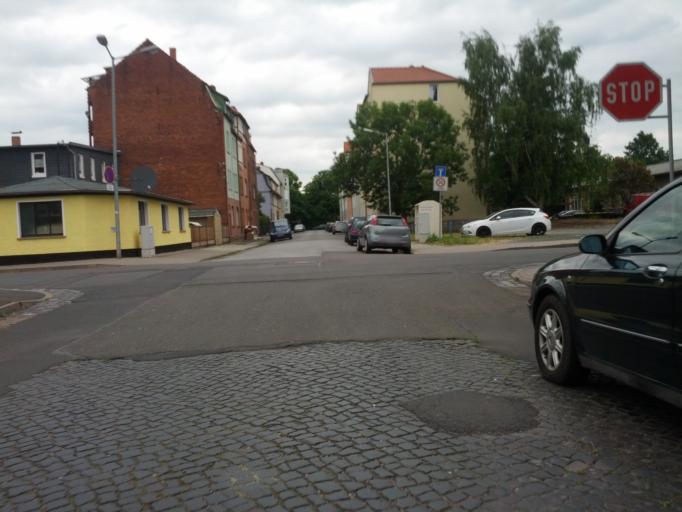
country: DE
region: Thuringia
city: Eisenach
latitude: 50.9817
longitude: 10.3122
